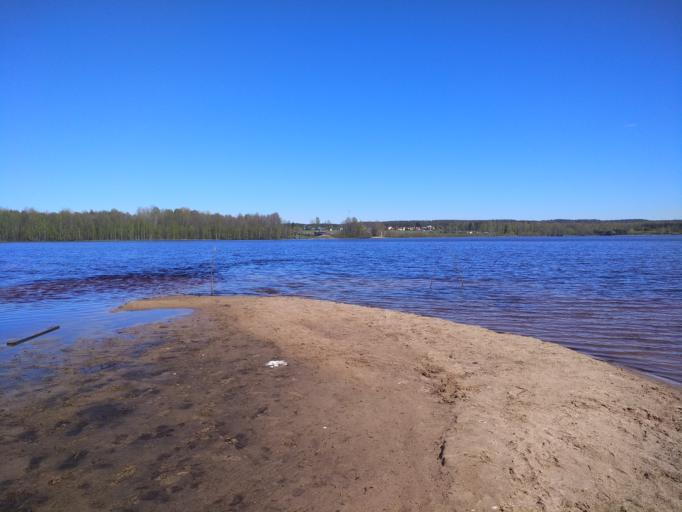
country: RU
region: Leningrad
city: Yakovlevo
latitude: 60.4461
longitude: 29.4475
